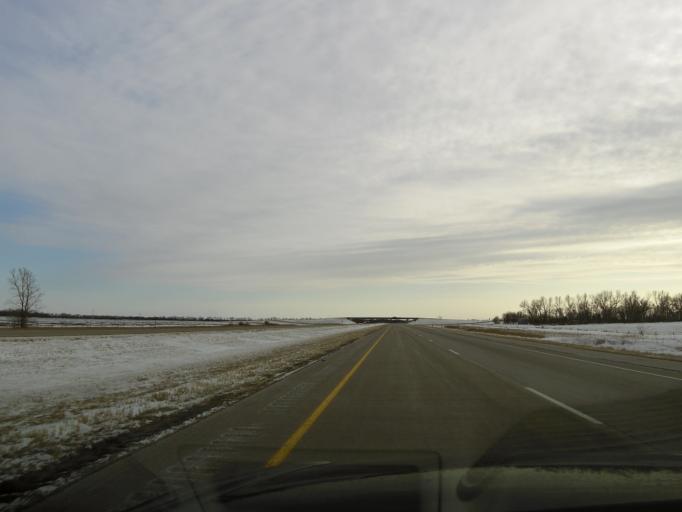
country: US
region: North Dakota
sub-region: Walsh County
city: Grafton
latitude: 48.4758
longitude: -97.1906
